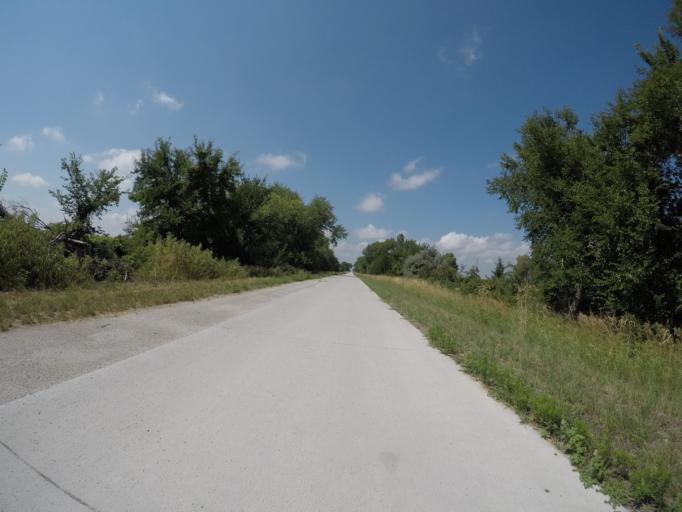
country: US
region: Nebraska
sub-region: Buffalo County
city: Kearney
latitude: 40.6636
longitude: -98.9883
